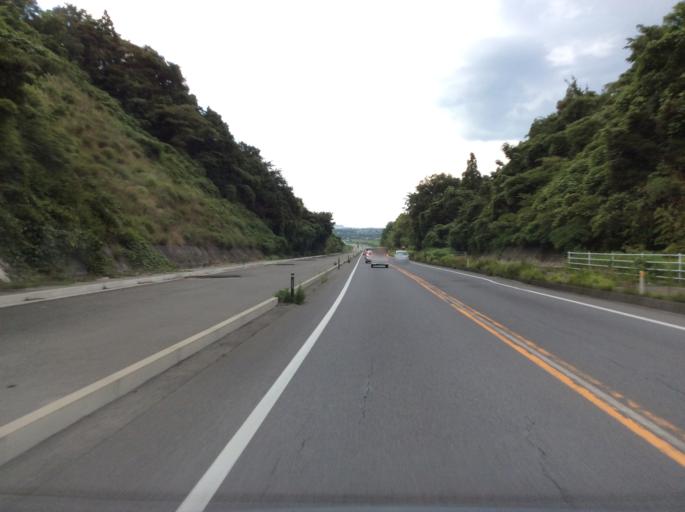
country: JP
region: Fukushima
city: Iwaki
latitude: 37.0440
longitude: 140.9363
